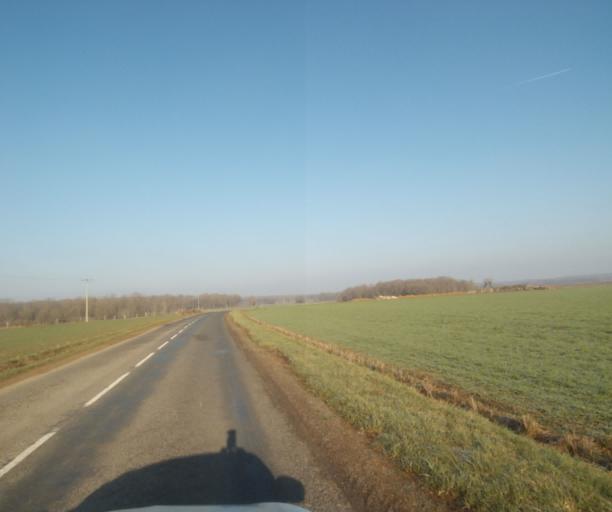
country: FR
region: Champagne-Ardenne
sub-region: Departement de la Haute-Marne
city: Montier-en-Der
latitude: 48.4998
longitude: 4.7513
